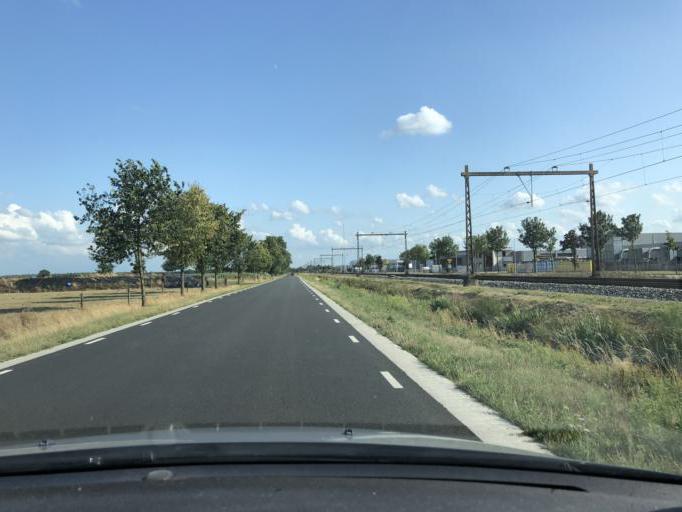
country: NL
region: Overijssel
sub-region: Gemeente Staphorst
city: Staphorst
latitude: 52.6399
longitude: 6.2260
